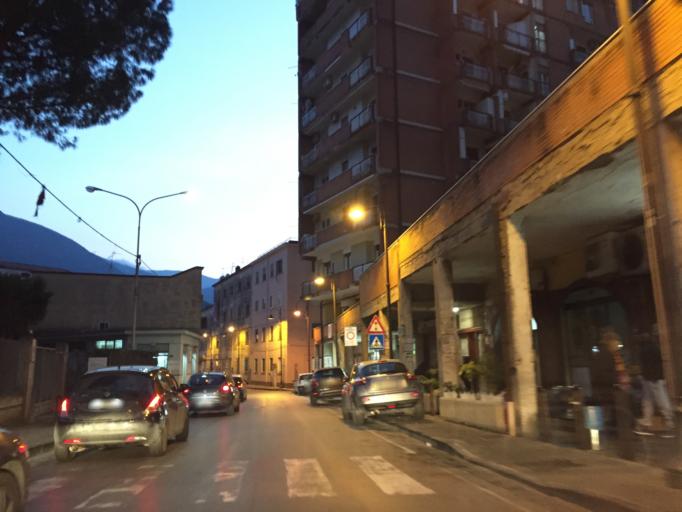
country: IT
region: Campania
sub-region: Provincia di Salerno
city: Nocera Inferiore
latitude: 40.7476
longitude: 14.6376
